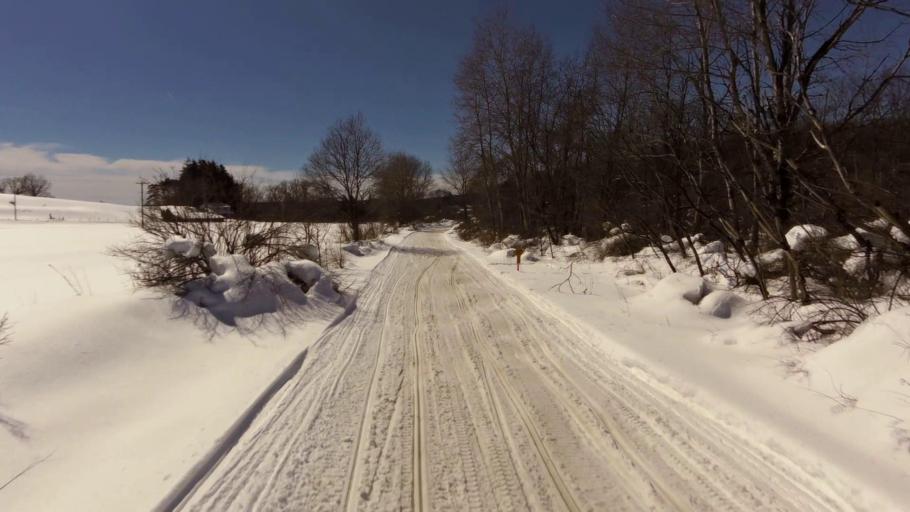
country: US
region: New York
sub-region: Cattaraugus County
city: Franklinville
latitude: 42.4104
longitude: -78.4684
